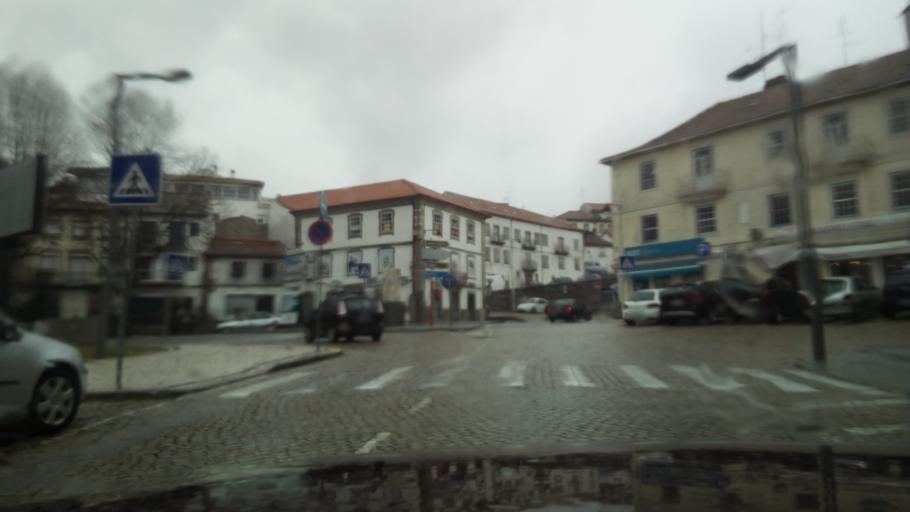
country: PT
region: Guarda
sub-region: Guarda
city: Guarda
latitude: 40.5362
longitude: -7.2678
